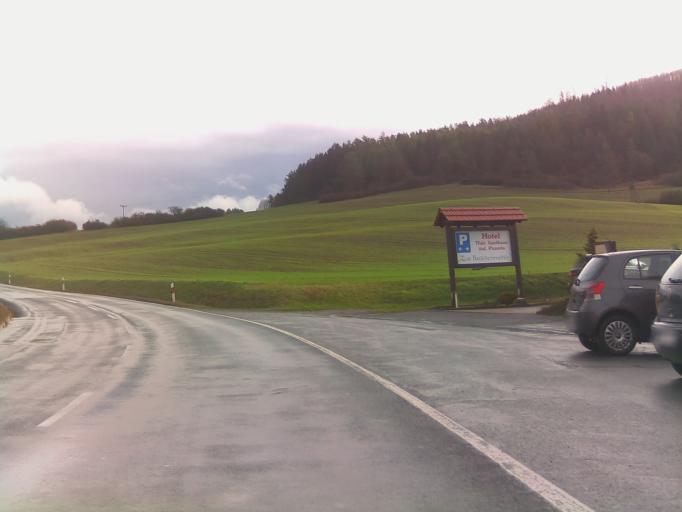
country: DE
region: Thuringia
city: Walldorf
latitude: 50.6035
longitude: 10.3794
